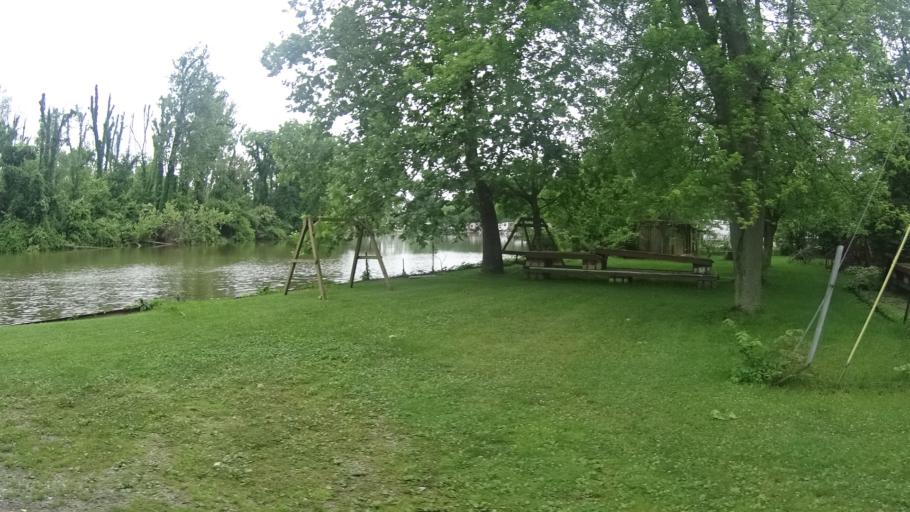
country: US
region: Ohio
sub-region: Erie County
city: Huron
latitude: 41.3547
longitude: -82.5585
